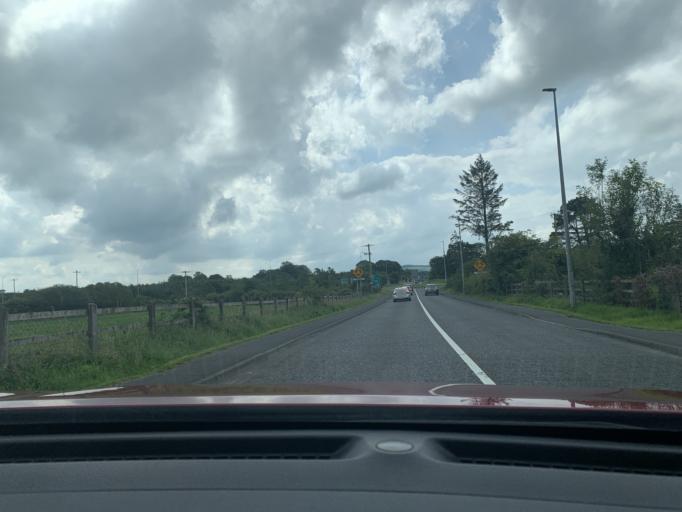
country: IE
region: Connaught
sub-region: Sligo
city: Tobercurry
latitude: 53.9523
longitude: -8.7931
